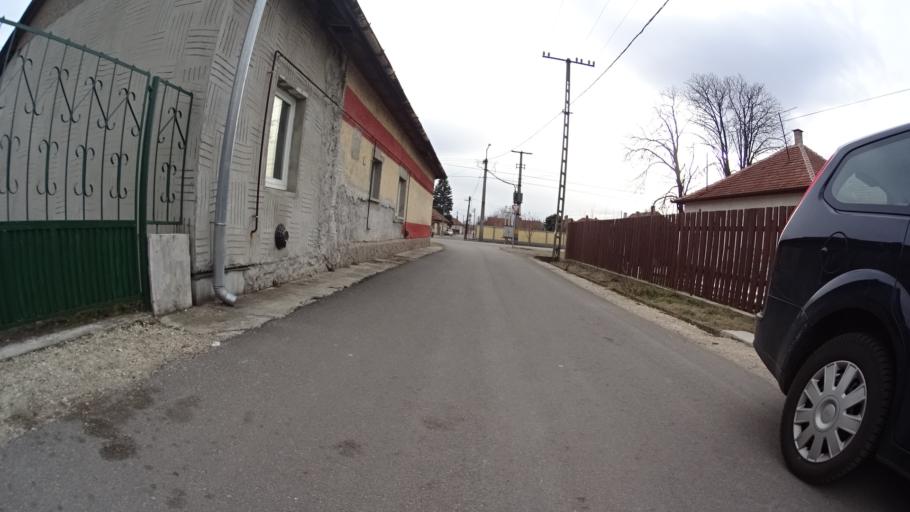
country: HU
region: Bacs-Kiskun
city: Tiszakecske
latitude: 46.9357
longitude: 20.0881
